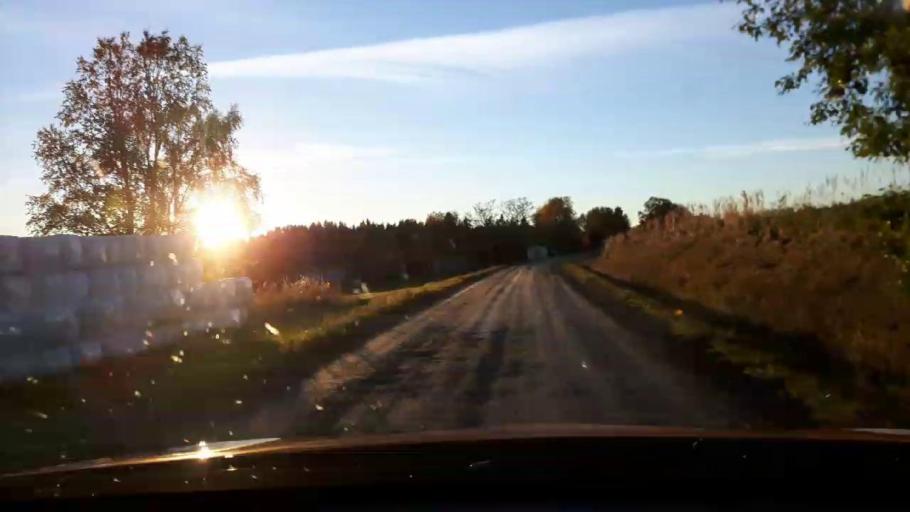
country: SE
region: Jaemtland
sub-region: Krokoms Kommun
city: Krokom
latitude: 63.4800
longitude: 14.2938
